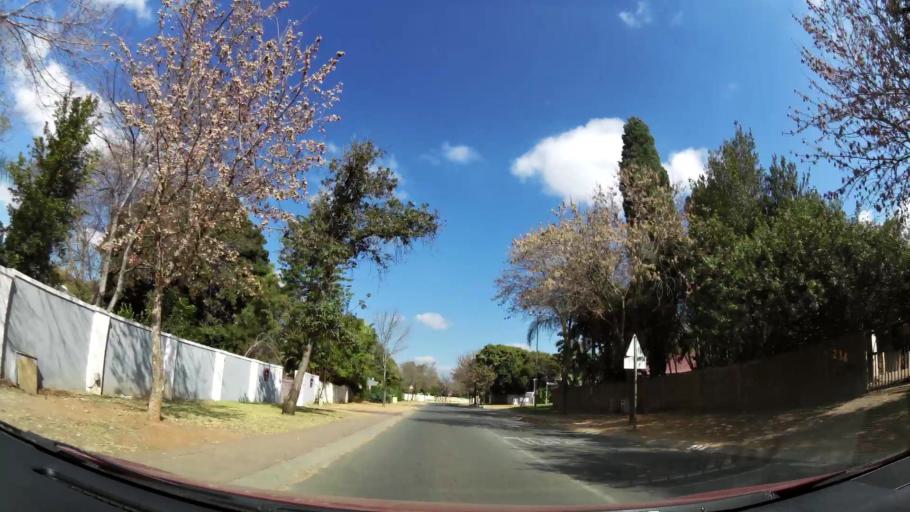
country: ZA
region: Gauteng
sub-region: West Rand District Municipality
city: Muldersdriseloop
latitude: -26.0631
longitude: 27.9618
